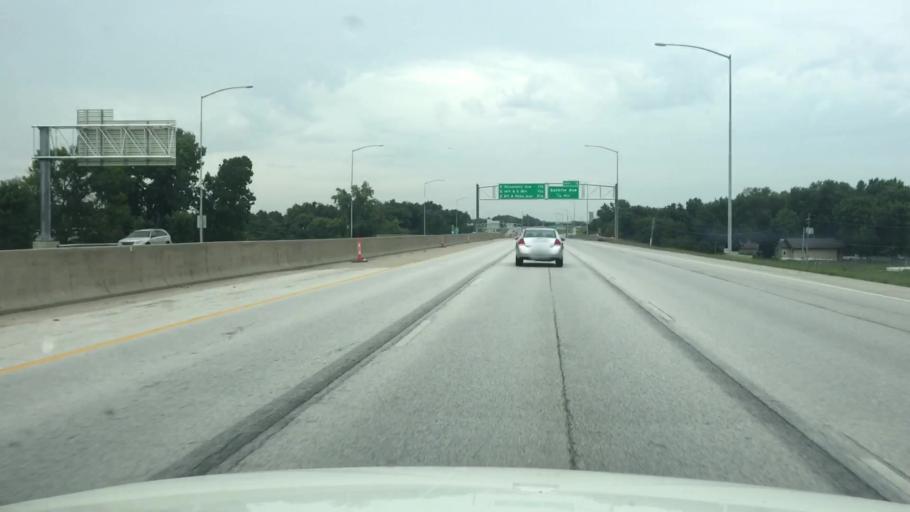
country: US
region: Iowa
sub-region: Polk County
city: Des Moines
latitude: 41.6240
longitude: -93.5759
